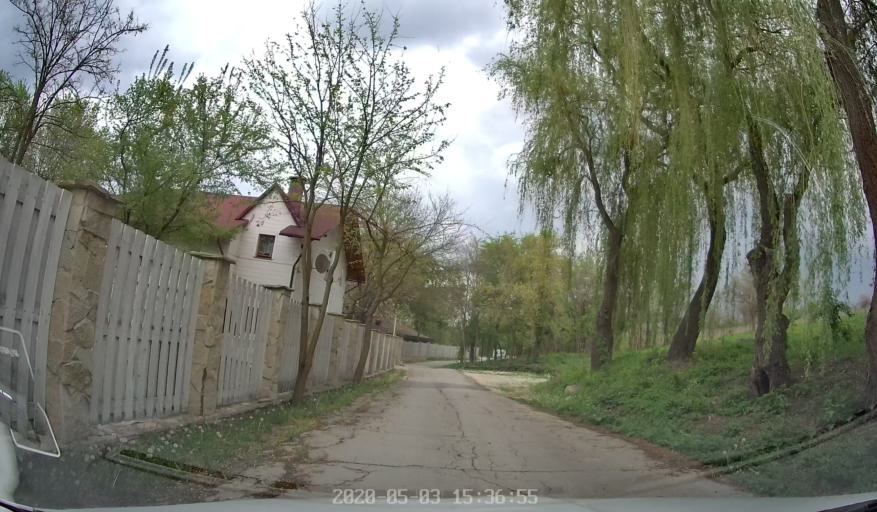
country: MD
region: Chisinau
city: Vatra
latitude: 47.1002
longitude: 28.7052
